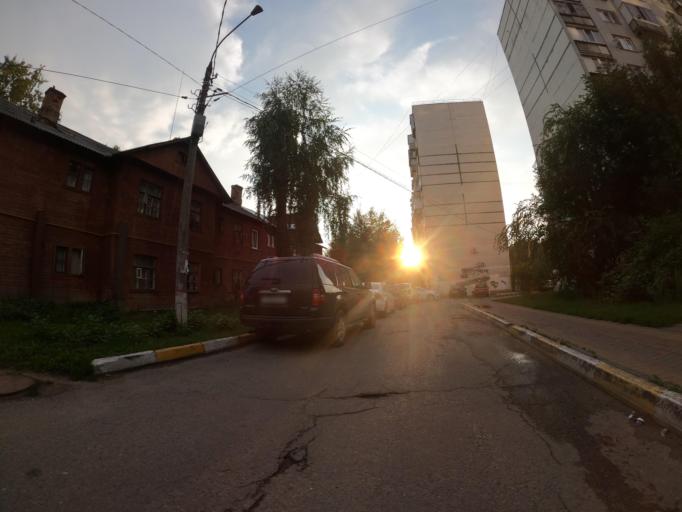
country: RU
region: Moskovskaya
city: Bykovo
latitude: 55.6418
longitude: 38.0864
